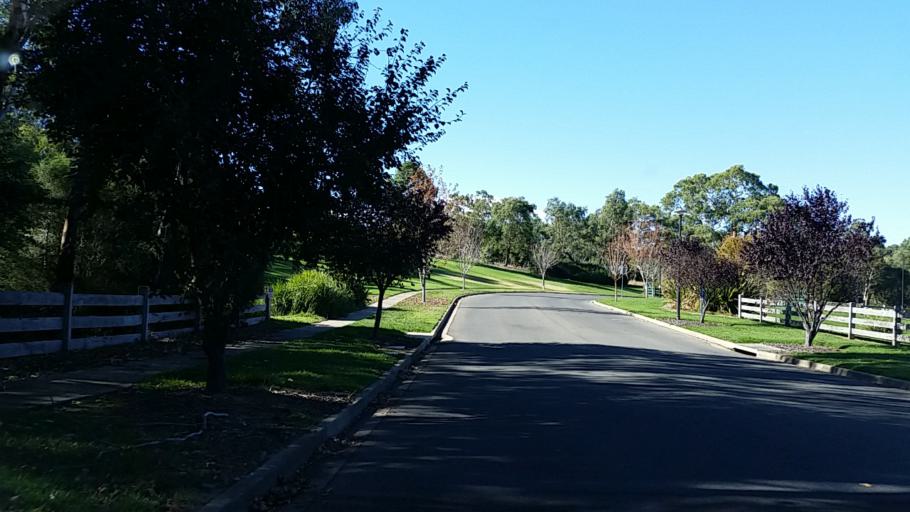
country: AU
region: South Australia
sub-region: Mount Barker
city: Mount Barker
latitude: -35.0655
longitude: 138.8902
